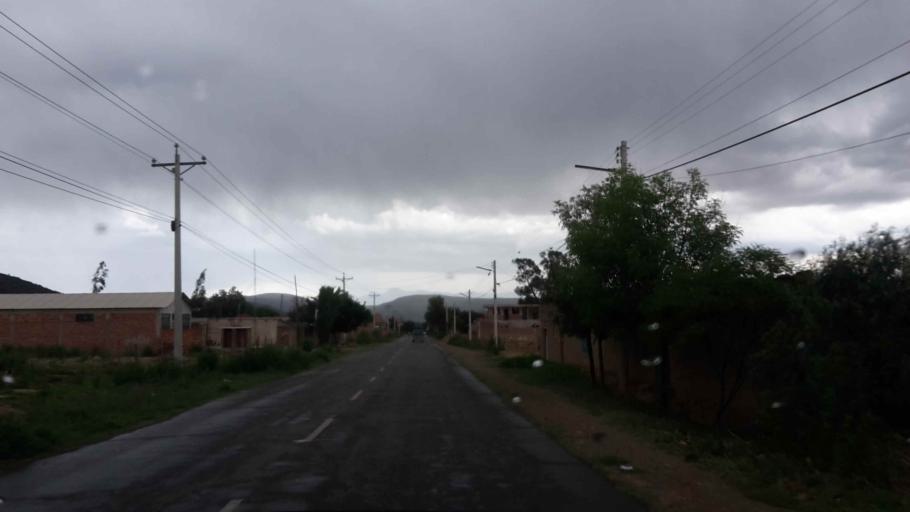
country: BO
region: Cochabamba
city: Tarata
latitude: -17.5815
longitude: -66.0553
